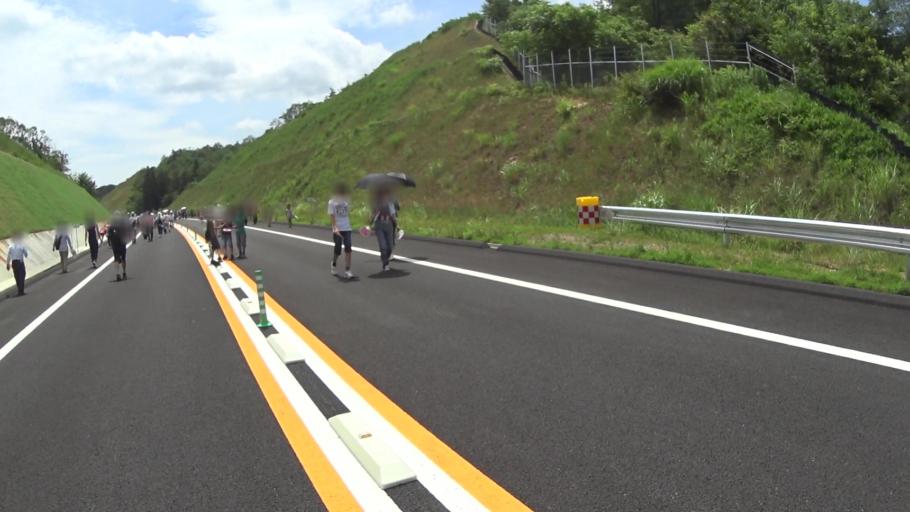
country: JP
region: Kyoto
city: Ayabe
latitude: 35.1699
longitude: 135.3720
